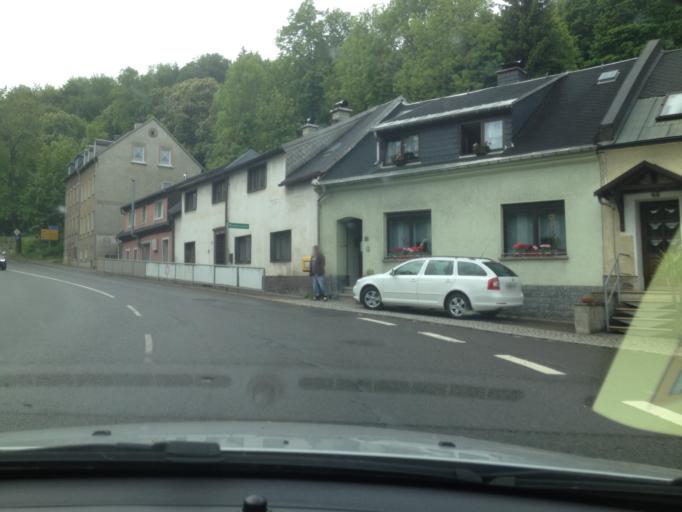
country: DE
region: Saxony
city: Annaberg-Buchholz
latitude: 50.5601
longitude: 12.9985
